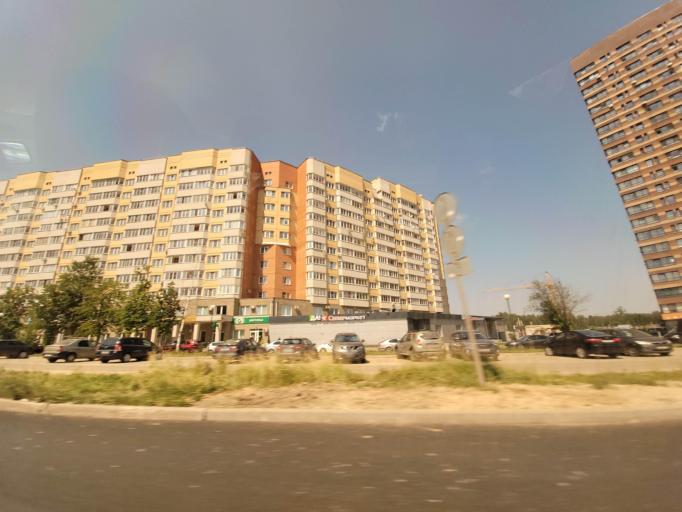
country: RU
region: Kaluga
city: Obninsk
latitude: 55.1234
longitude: 36.6099
